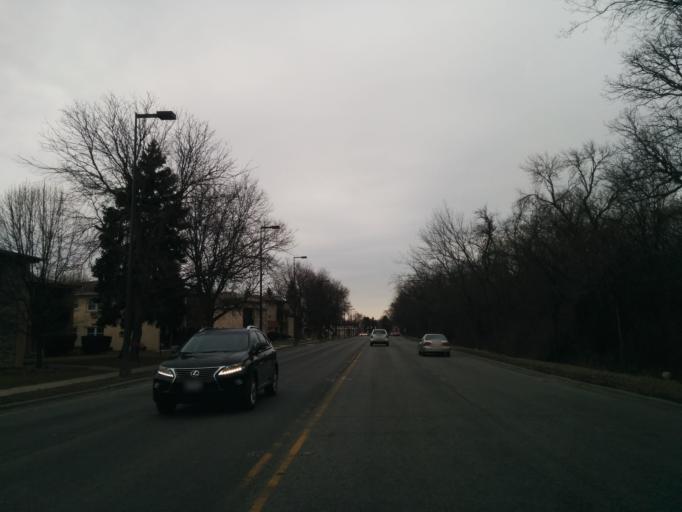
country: US
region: Illinois
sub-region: Cook County
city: La Grange Park
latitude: 41.8375
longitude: -87.8757
